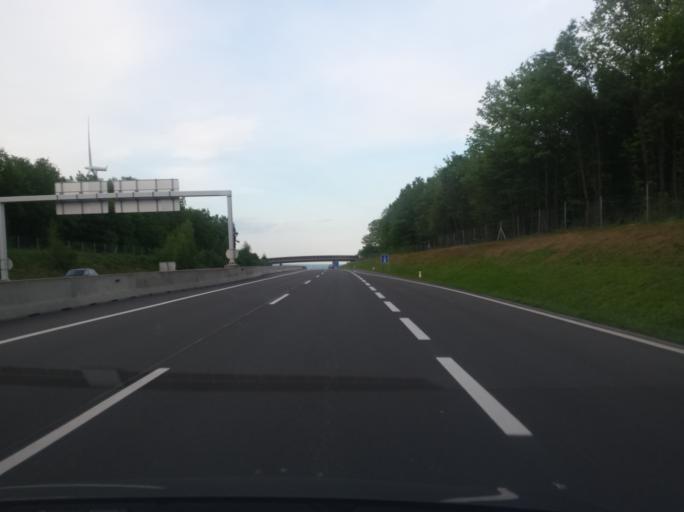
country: AT
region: Burgenland
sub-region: Politischer Bezirk Mattersburg
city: Pottelsdorf
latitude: 47.7586
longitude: 16.4122
